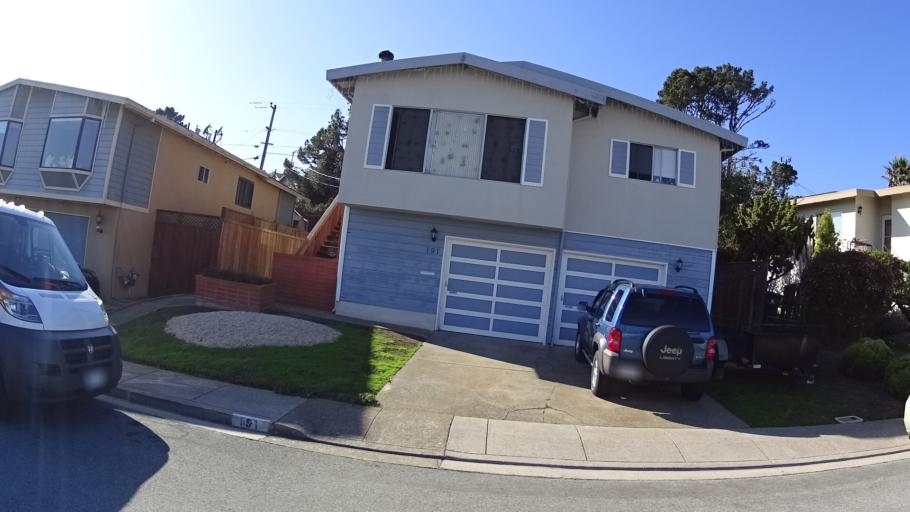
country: US
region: California
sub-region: San Mateo County
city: Pacifica
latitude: 37.6304
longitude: -122.4554
